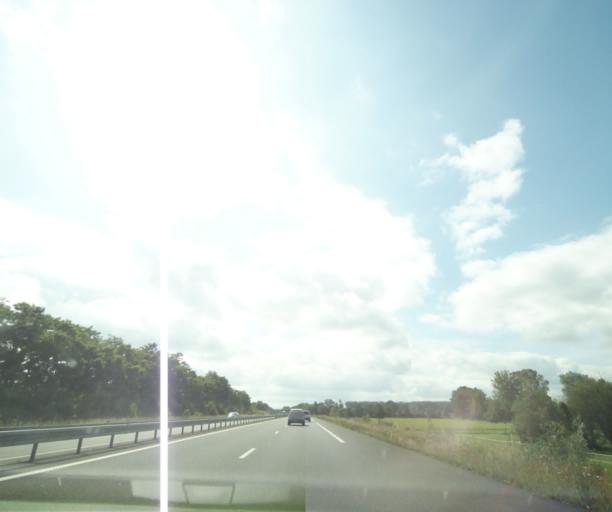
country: FR
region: Pays de la Loire
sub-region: Departement de Maine-et-Loire
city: Jumelles
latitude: 47.3952
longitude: -0.1121
